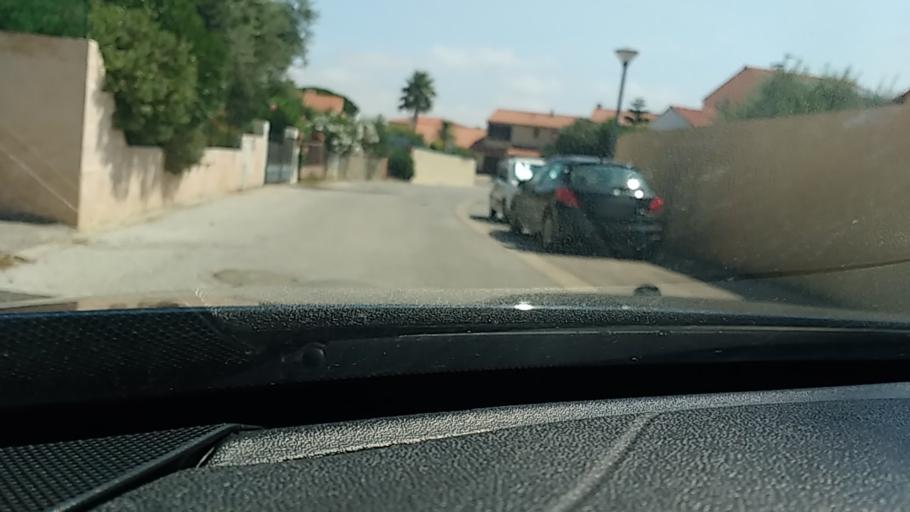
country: FR
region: Languedoc-Roussillon
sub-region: Departement des Pyrenees-Orientales
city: Villeneuve-de-la-Raho
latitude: 42.6327
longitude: 2.9193
